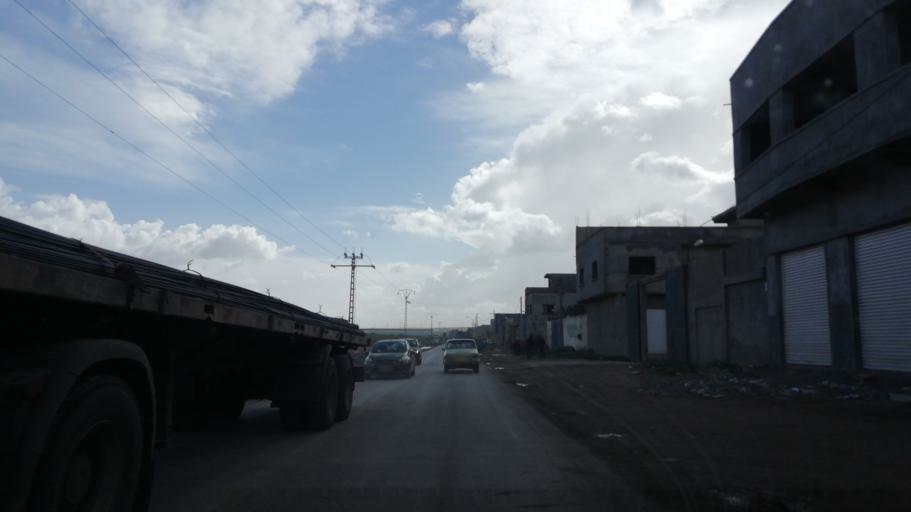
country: DZ
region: Oran
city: Sidi ech Chahmi
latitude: 35.6465
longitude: -0.5600
